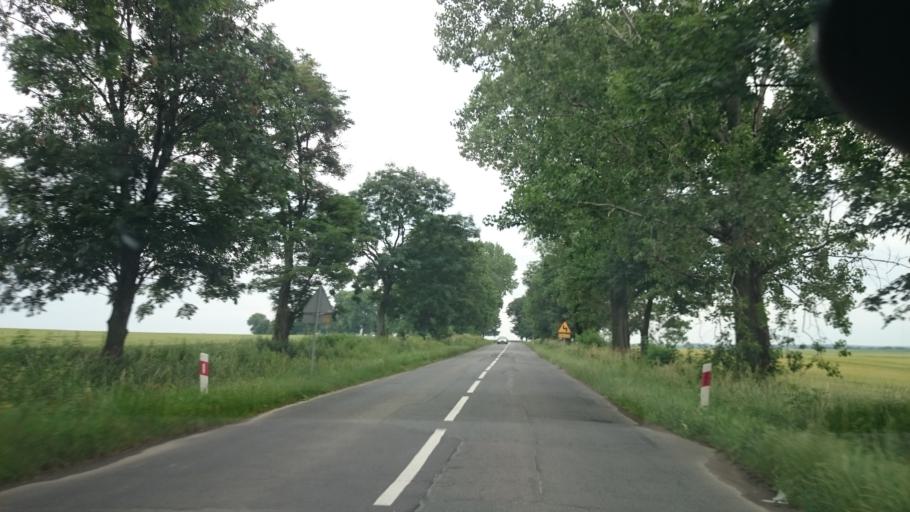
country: PL
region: Lower Silesian Voivodeship
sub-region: Powiat zabkowicki
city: Kamieniec Zabkowicki
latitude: 50.5824
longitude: 16.8985
